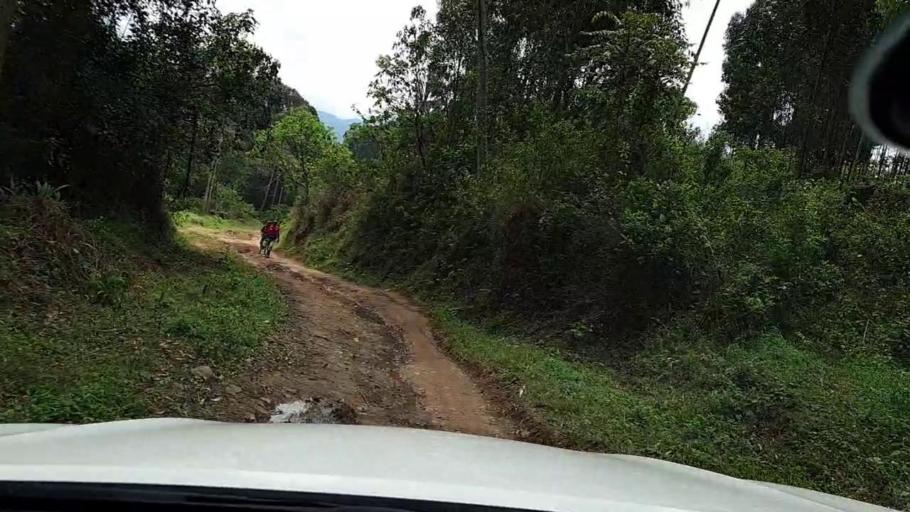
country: RW
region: Western Province
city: Kibuye
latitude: -2.2835
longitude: 29.3046
